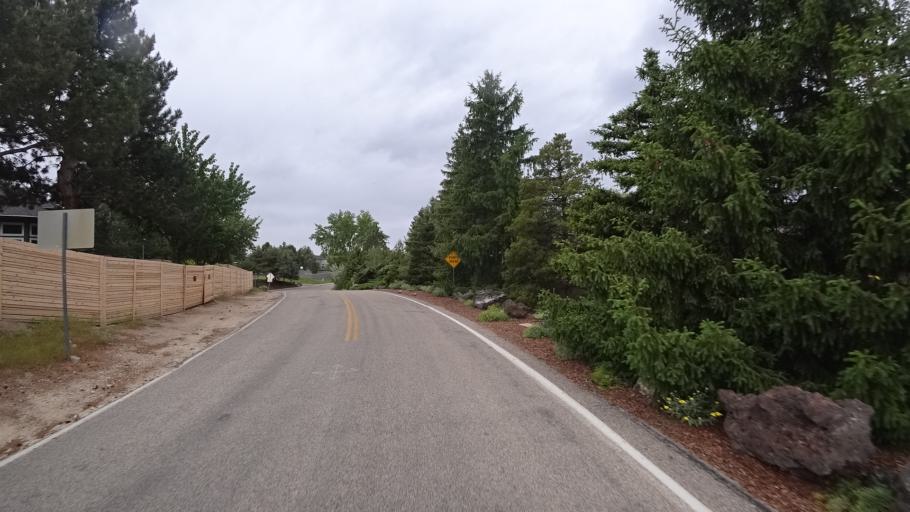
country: US
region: Idaho
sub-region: Ada County
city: Boise
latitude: 43.6176
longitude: -116.1677
